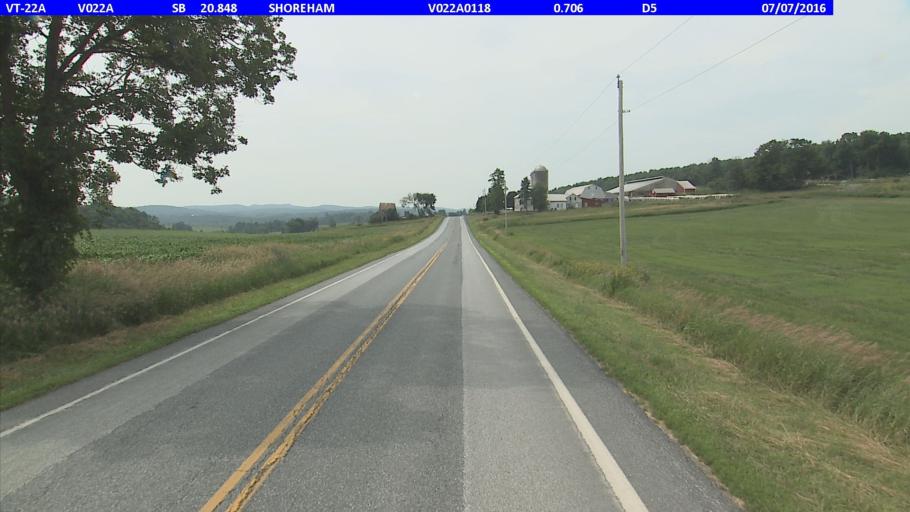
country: US
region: New York
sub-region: Essex County
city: Ticonderoga
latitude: 43.8596
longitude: -73.3095
